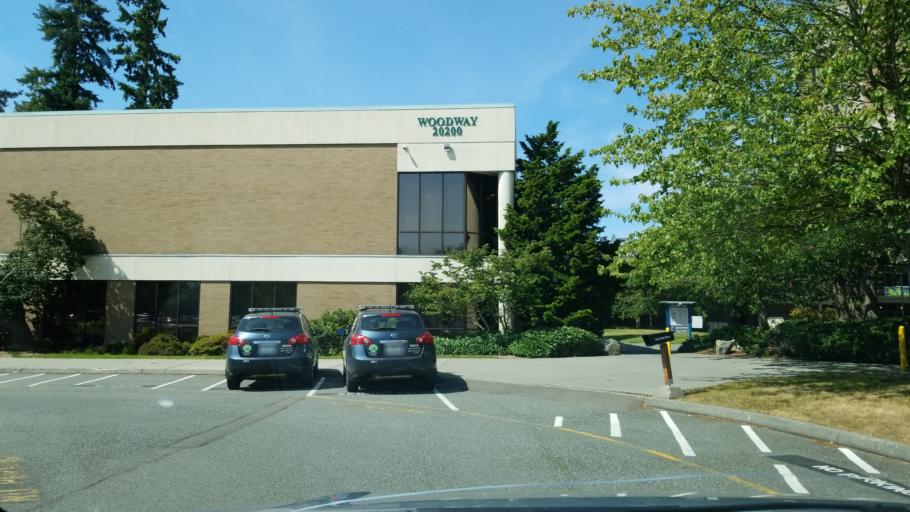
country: US
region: Washington
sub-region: Snohomish County
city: Lynnwood
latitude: 47.8154
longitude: -122.3284
